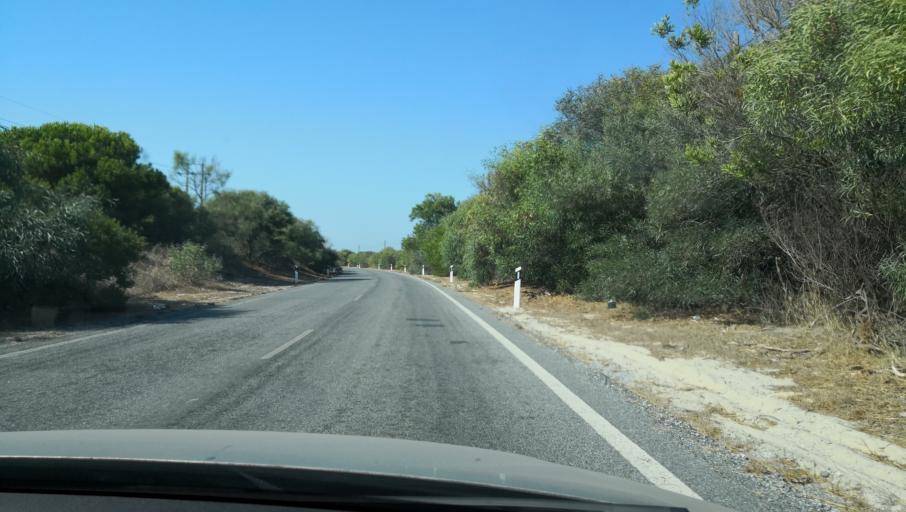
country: PT
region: Setubal
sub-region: Setubal
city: Setubal
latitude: 38.4016
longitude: -8.8069
